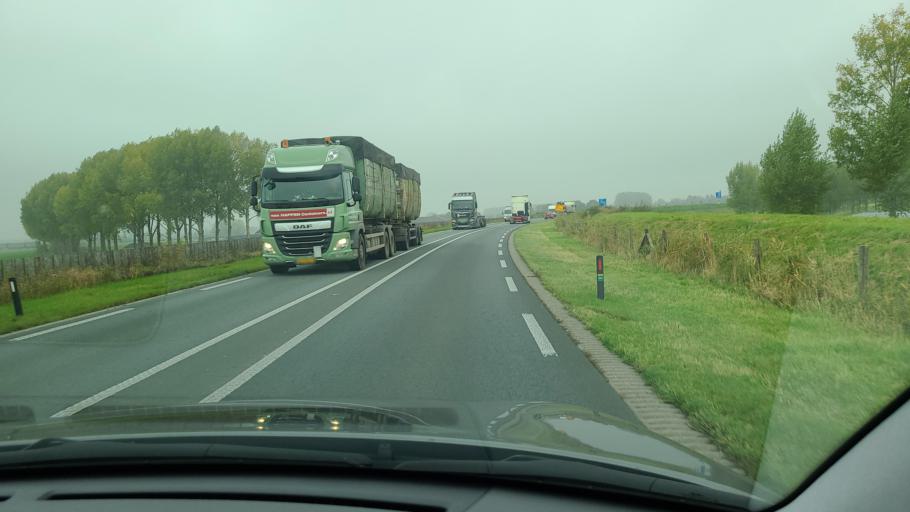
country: NL
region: Gelderland
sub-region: Gemeente Tiel
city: Tiel
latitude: 51.8709
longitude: 5.4997
